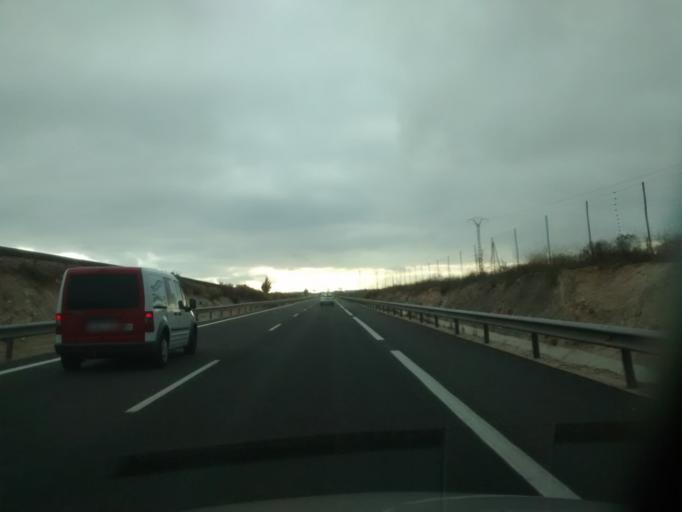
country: ES
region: Castille-La Mancha
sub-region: Provincia de Guadalajara
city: Trijueque
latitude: 40.7649
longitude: -3.0068
